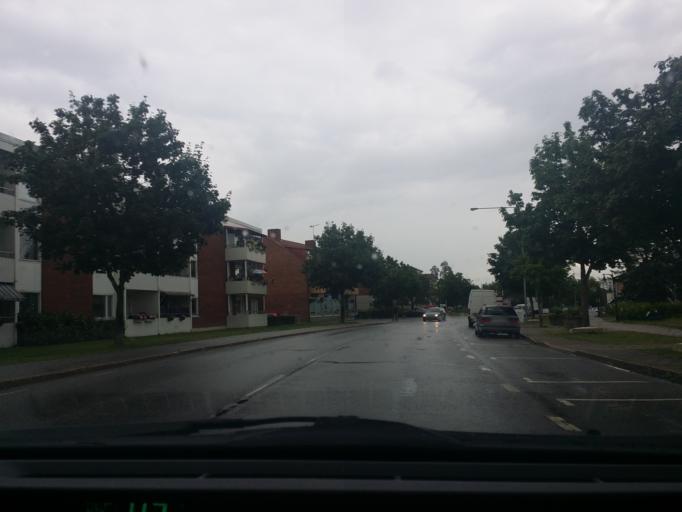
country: SE
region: OErebro
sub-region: Lindesbergs Kommun
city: Frovi
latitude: 59.4666
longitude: 15.3610
